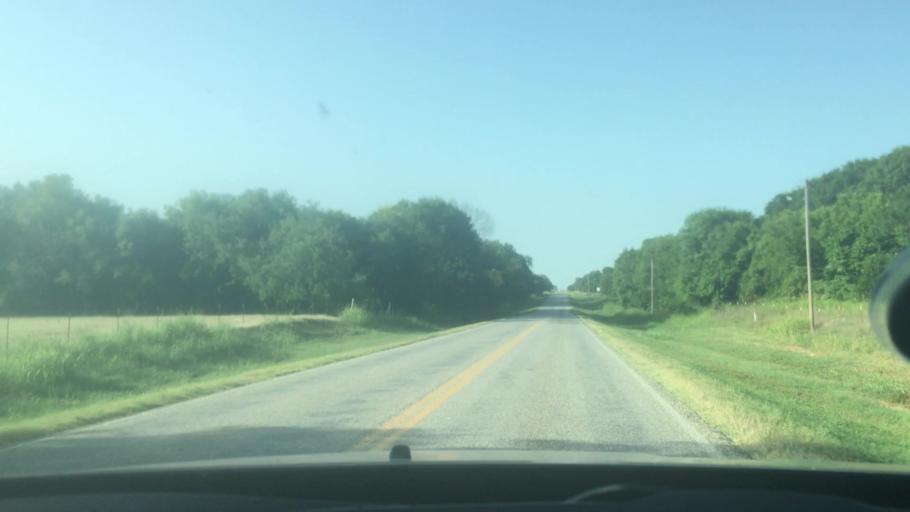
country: US
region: Oklahoma
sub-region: Johnston County
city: Tishomingo
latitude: 34.2997
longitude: -96.4248
